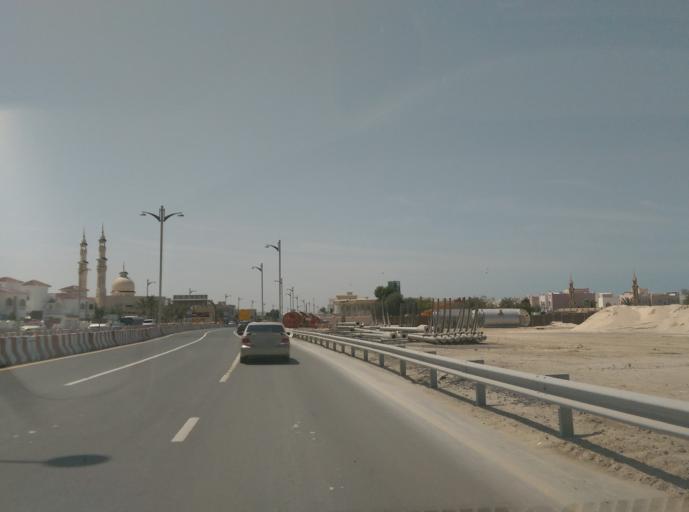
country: AE
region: Dubai
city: Dubai
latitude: 25.1933
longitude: 55.2336
